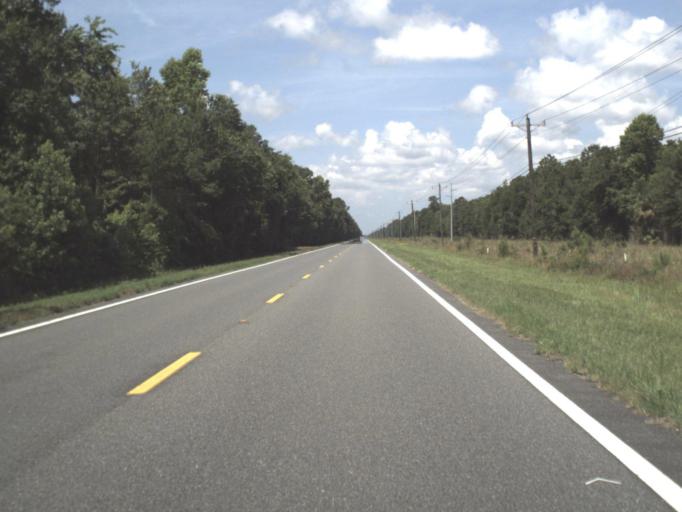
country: US
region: Florida
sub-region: Levy County
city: Chiefland
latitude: 29.2860
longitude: -82.8419
